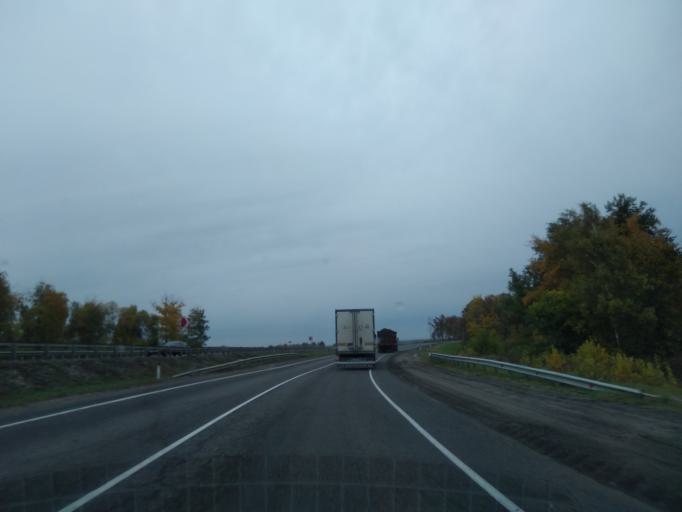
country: RU
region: Lipetsk
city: Zadonsk
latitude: 52.4454
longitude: 38.7853
